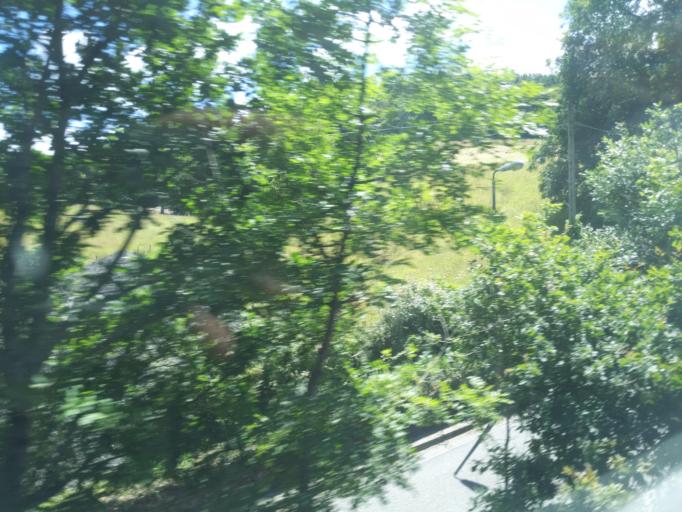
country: GB
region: England
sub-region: Cornwall
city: Lostwithiel
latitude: 50.4471
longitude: -4.6609
